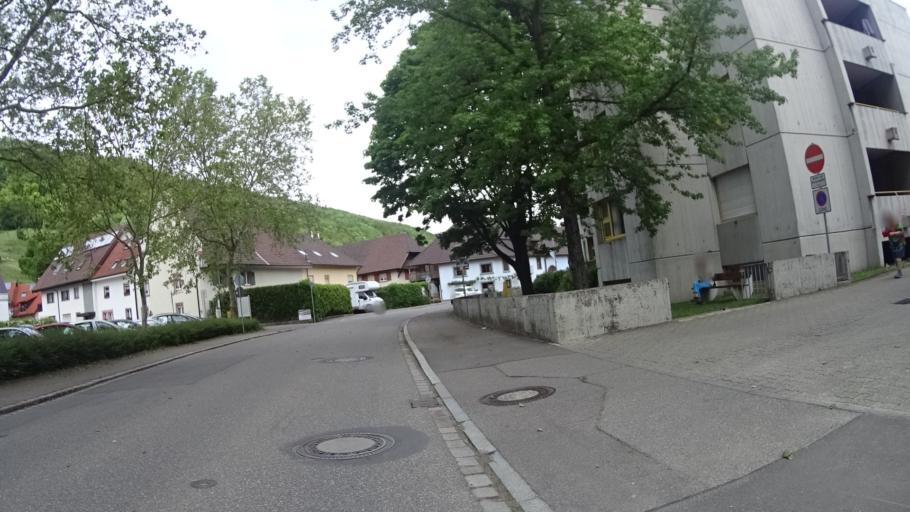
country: CH
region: Aargau
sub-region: Bezirk Rheinfelden
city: Kaiseraugst
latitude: 47.5559
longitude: 7.7297
